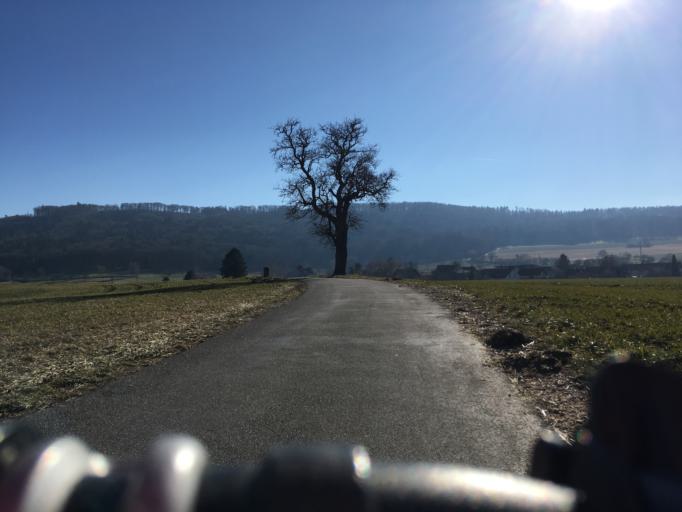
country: DE
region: Baden-Wuerttemberg
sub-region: Freiburg Region
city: Gottmadingen
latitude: 47.7182
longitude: 8.7696
